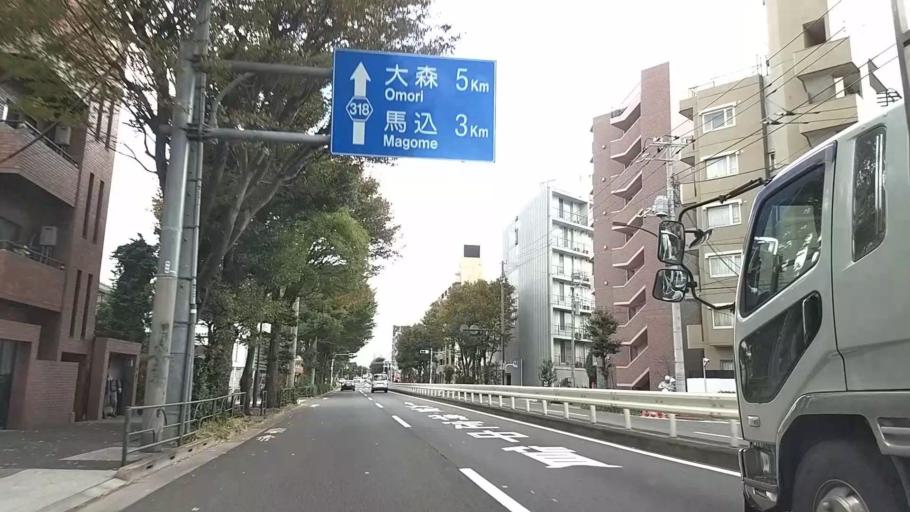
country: JP
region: Tokyo
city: Tokyo
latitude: 35.6105
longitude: 139.6912
